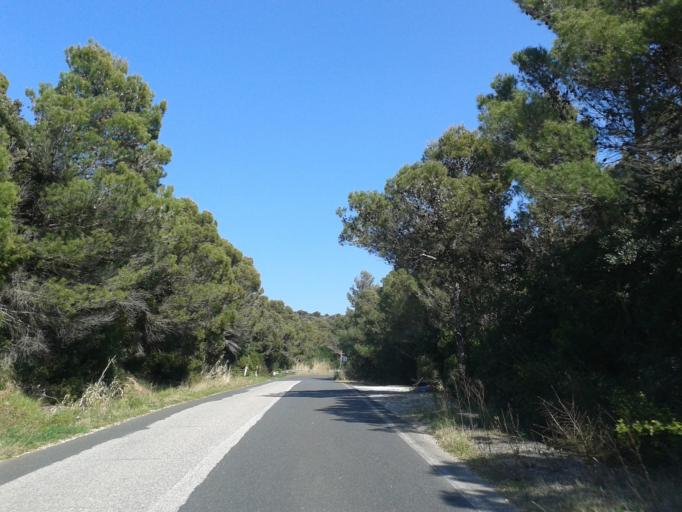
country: IT
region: Tuscany
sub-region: Provincia di Livorno
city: Quercianella
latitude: 43.4484
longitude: 10.3906
